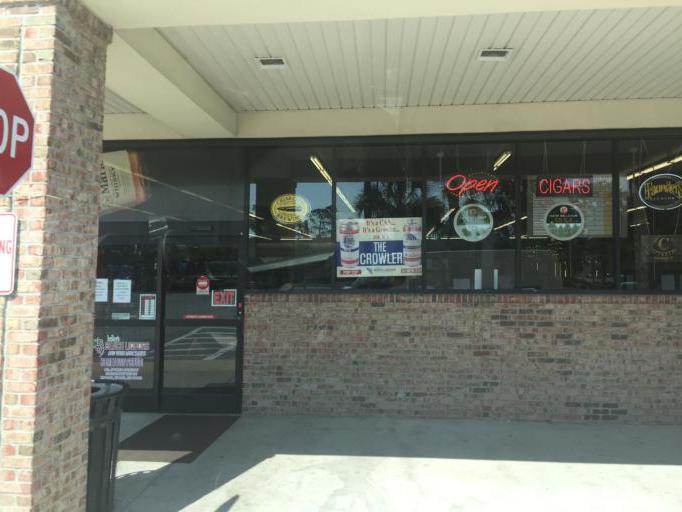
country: US
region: Florida
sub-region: Bay County
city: Upper Grand Lagoon
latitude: 30.1593
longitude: -85.7522
